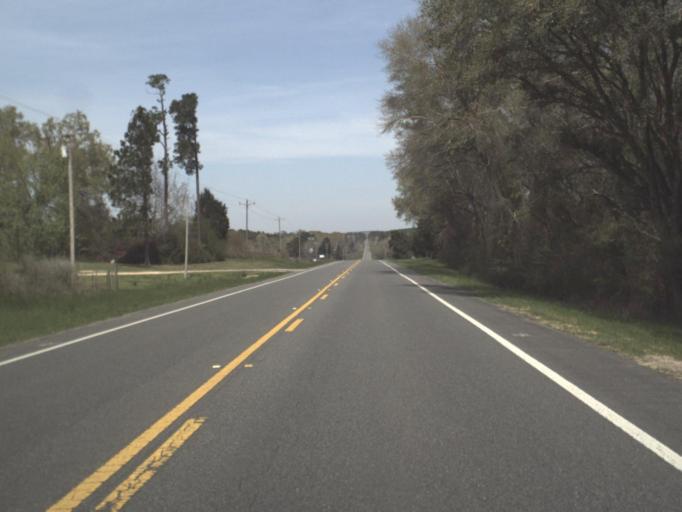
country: US
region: Florida
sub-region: Walton County
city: DeFuniak Springs
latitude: 30.7609
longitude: -85.9589
